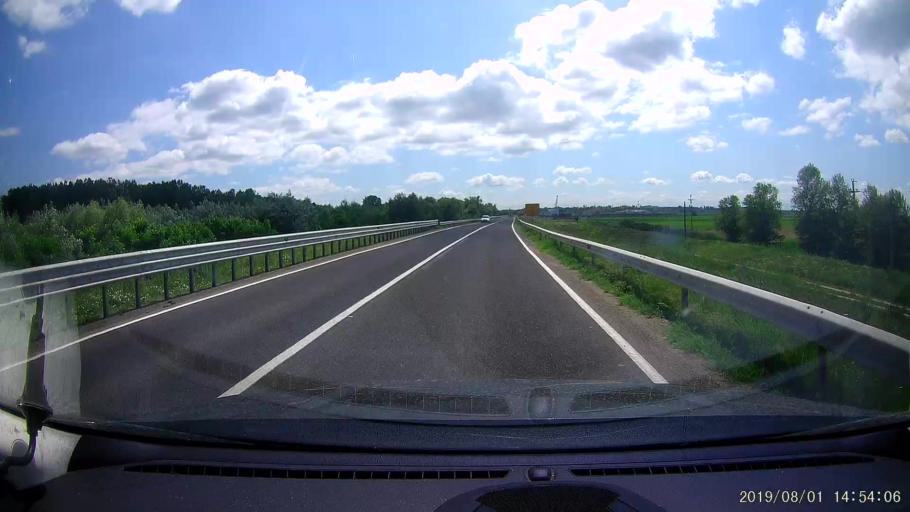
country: RO
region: Braila
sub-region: Municipiul Braila
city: Braila
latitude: 45.3232
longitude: 27.9945
